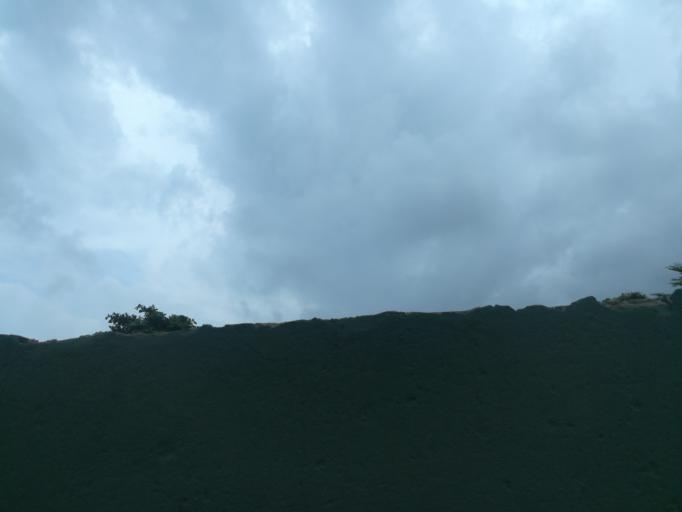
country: NG
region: Lagos
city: Oshodi
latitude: 6.5669
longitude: 3.3505
